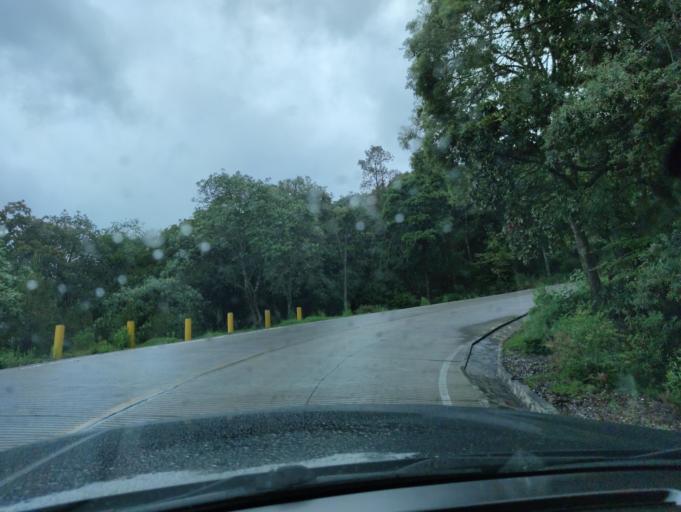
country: MX
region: Mexico
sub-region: Morelos
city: San Marcos Tlazalpan
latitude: 19.8746
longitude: -99.6575
